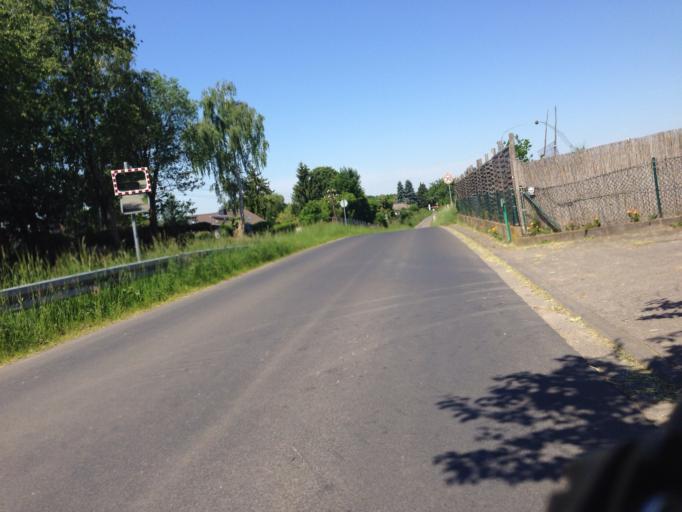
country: DE
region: Hesse
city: Budingen
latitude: 50.2794
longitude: 9.1154
